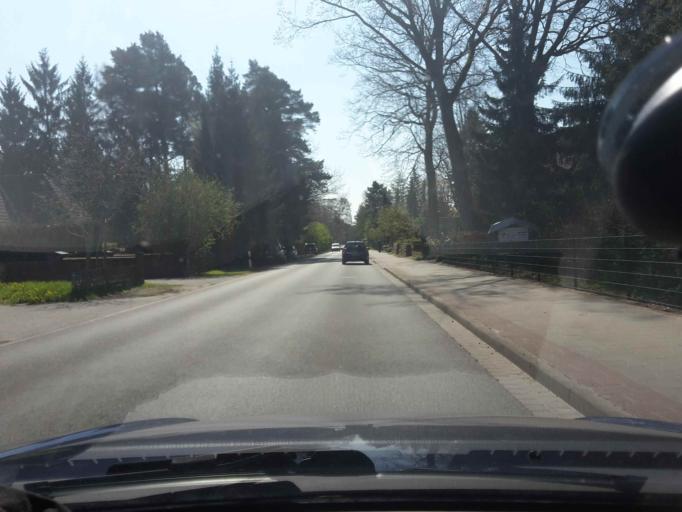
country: DE
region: Lower Saxony
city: Buchholz in der Nordheide
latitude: 53.2795
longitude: 9.8733
